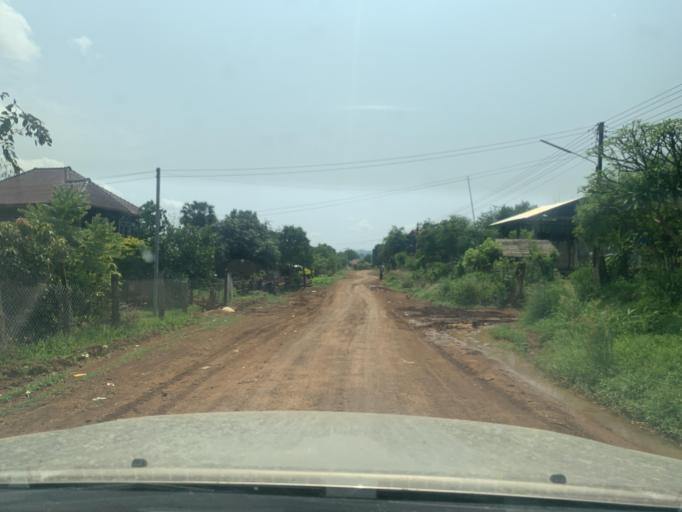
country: TH
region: Uttaradit
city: Ban Khok
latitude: 18.3622
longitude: 101.3903
